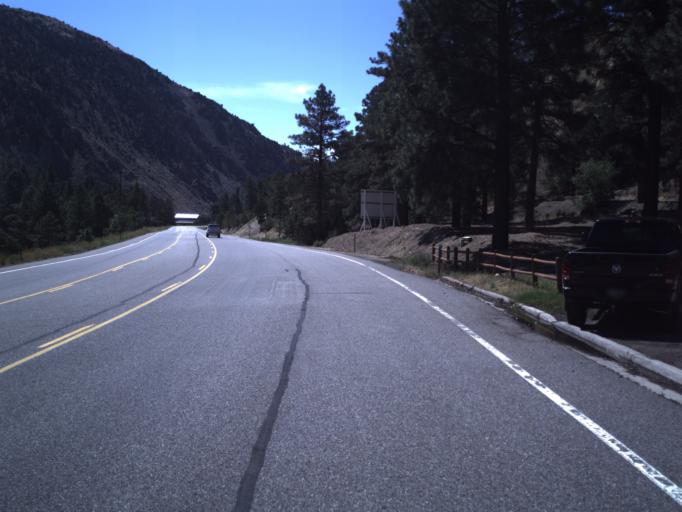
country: US
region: Utah
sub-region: Sevier County
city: Monroe
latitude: 38.5153
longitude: -112.2658
